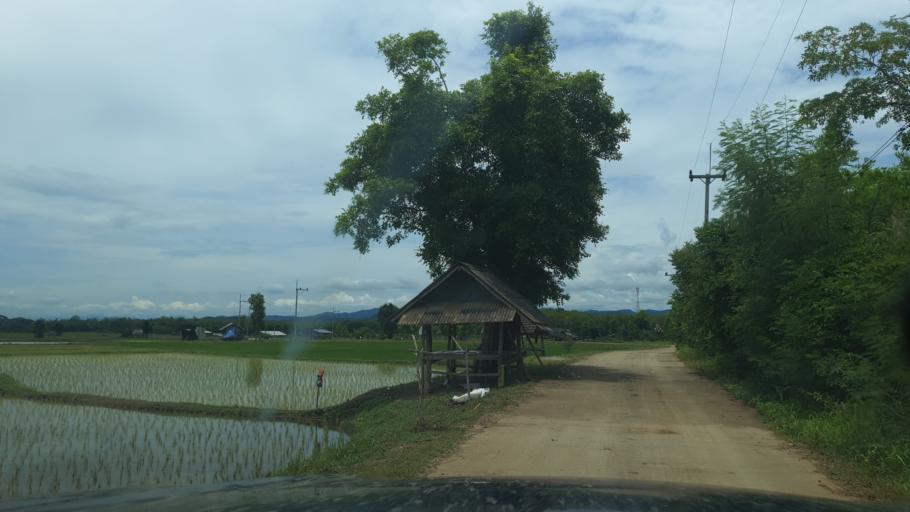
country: TH
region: Lampang
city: Ko Kha
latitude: 18.1293
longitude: 99.3424
